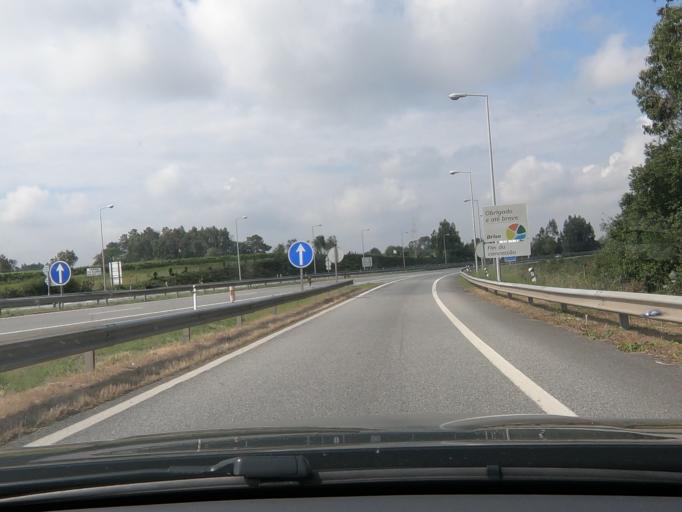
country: PT
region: Aveiro
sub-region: Albergaria-A-Velha
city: Albergaria-a-Velha
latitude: 40.6845
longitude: -8.5266
